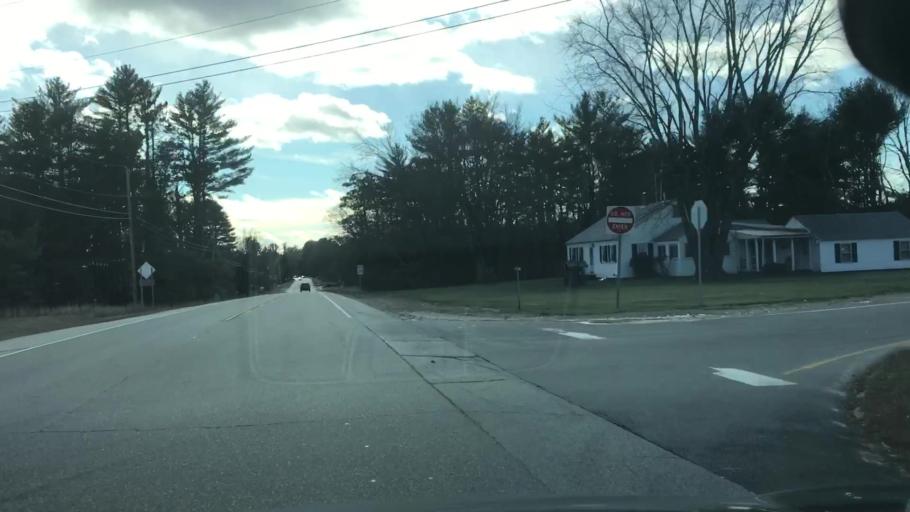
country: US
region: New Hampshire
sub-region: Merrimack County
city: Chichester
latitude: 43.2575
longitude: -71.3725
